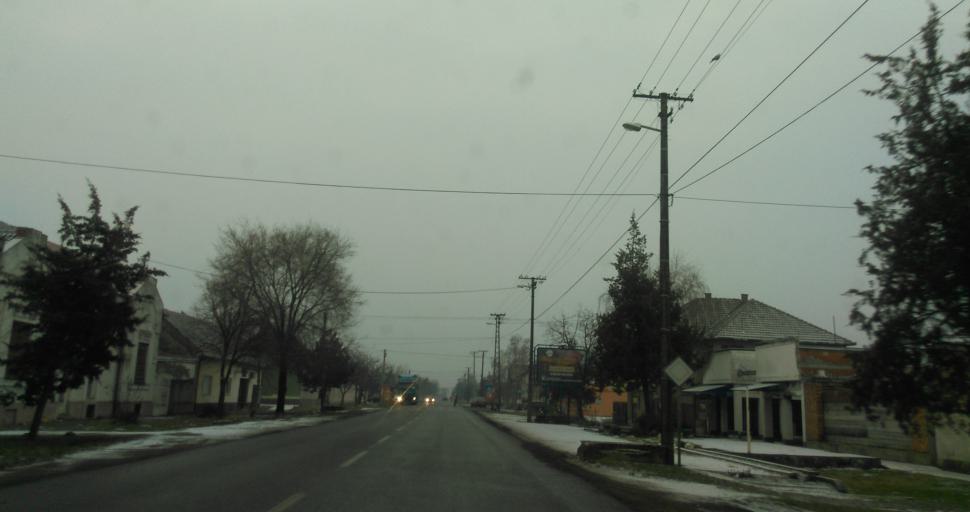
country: RS
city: Melenci
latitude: 45.5135
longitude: 20.3173
